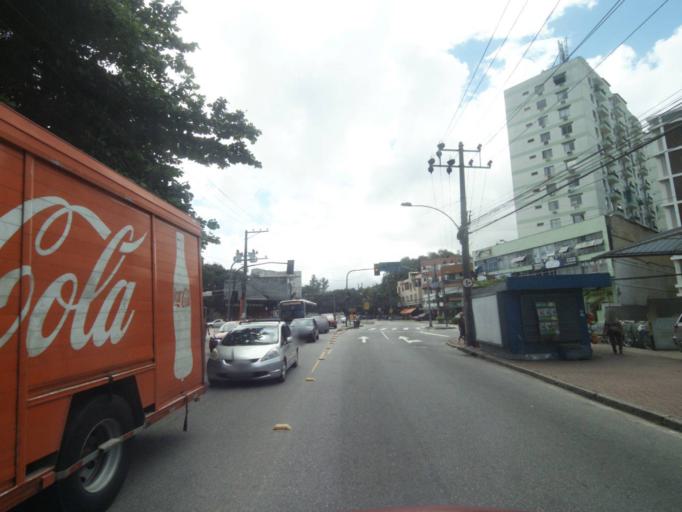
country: BR
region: Rio de Janeiro
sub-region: Sao Joao De Meriti
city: Sao Joao de Meriti
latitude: -22.9213
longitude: -43.3605
